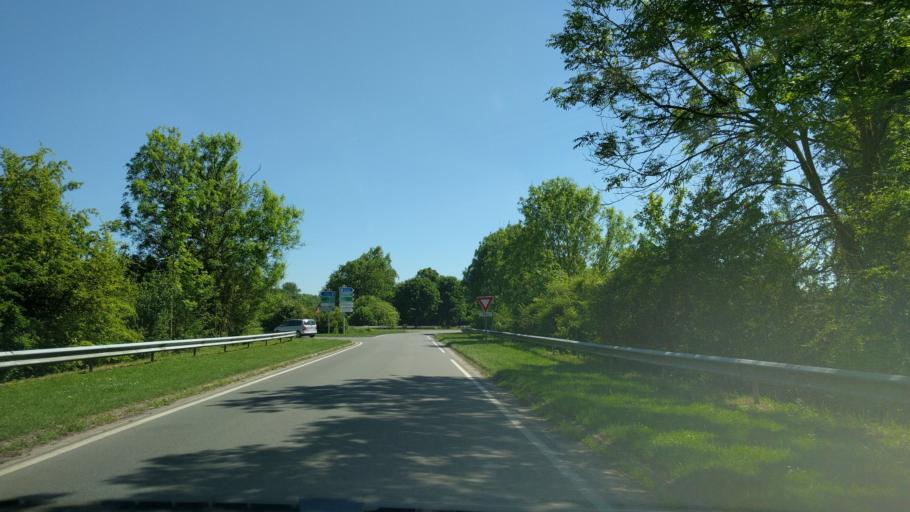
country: FR
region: Picardie
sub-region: Departement de la Somme
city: Peronne
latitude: 49.9362
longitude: 2.9471
